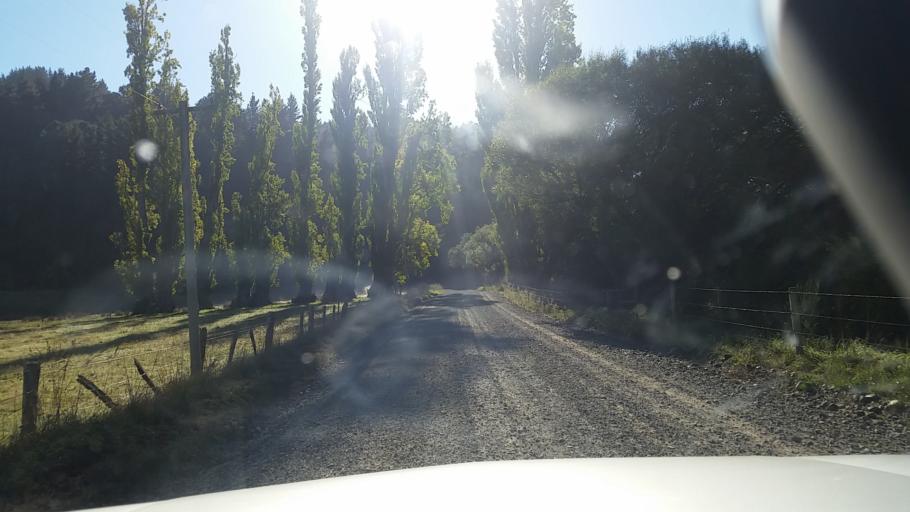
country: NZ
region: Marlborough
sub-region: Marlborough District
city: Blenheim
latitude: -41.4478
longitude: 173.8781
